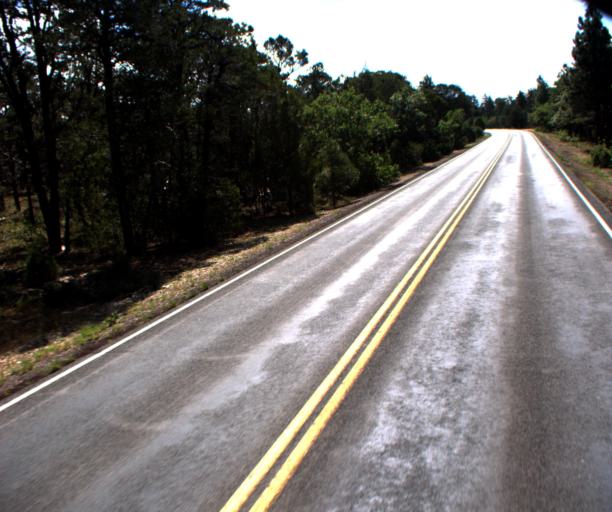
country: US
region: Arizona
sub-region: Coconino County
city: Grand Canyon
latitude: 35.9972
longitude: -112.0335
